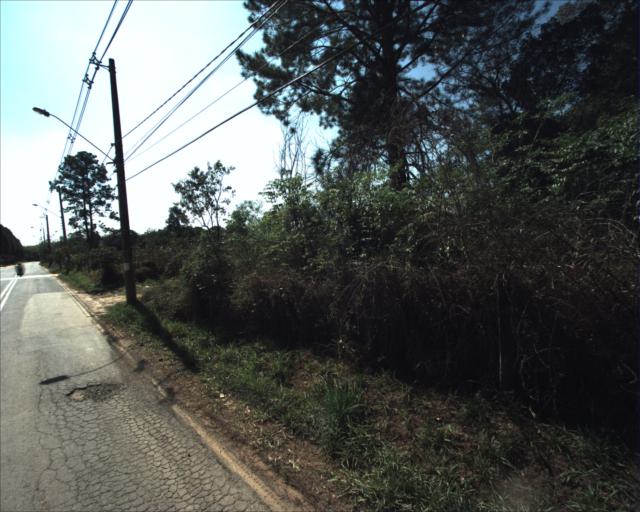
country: BR
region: Sao Paulo
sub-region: Aracoiaba Da Serra
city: Aracoiaba da Serra
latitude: -23.4797
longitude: -47.5404
